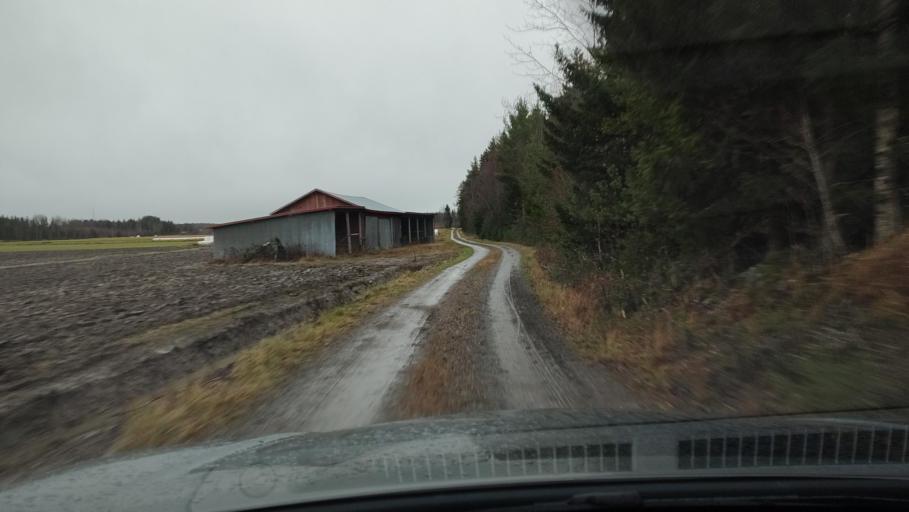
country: FI
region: Southern Ostrobothnia
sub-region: Suupohja
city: Karijoki
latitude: 62.2308
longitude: 21.5516
